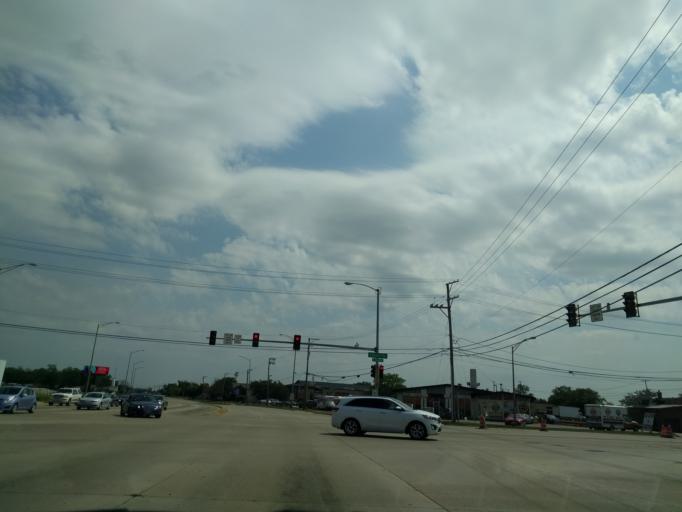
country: US
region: Illinois
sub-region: Cook County
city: Elk Grove Village
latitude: 42.0082
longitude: -87.9407
